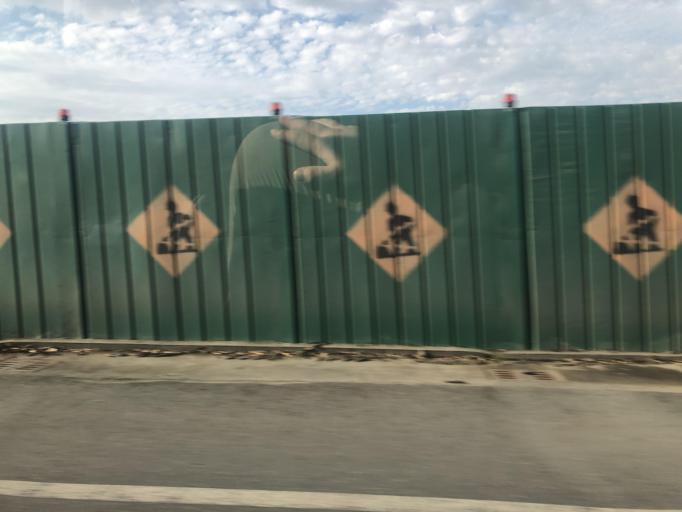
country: TW
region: Taiwan
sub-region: Tainan
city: Tainan
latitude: 23.0300
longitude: 120.1974
